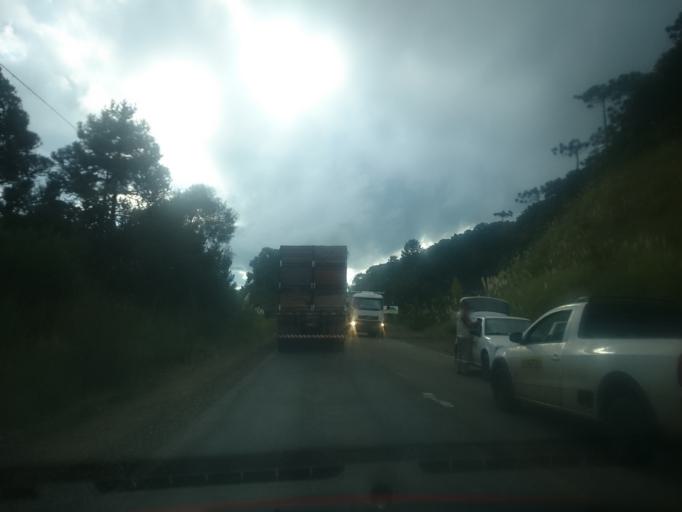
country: BR
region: Santa Catarina
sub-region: Sao Joaquim
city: Sao Joaquim
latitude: -28.3305
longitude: -49.7044
